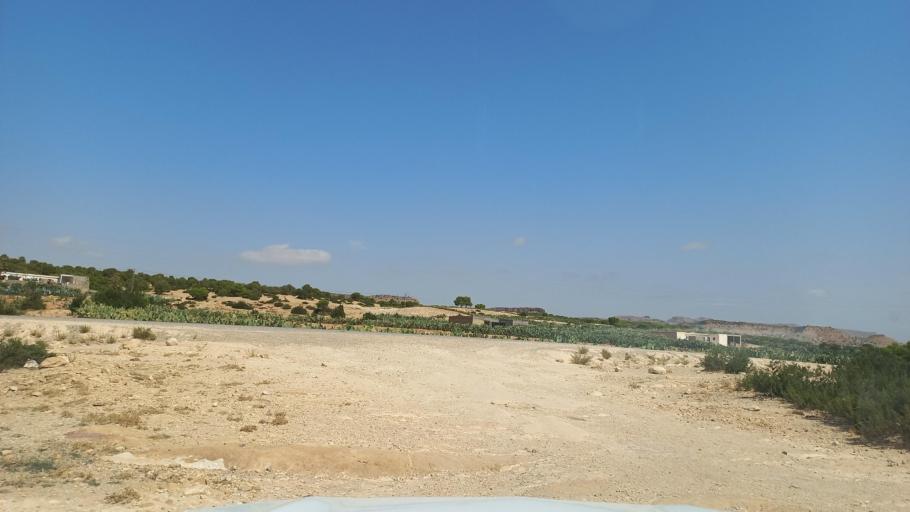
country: TN
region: Al Qasrayn
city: Sbiba
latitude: 35.3984
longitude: 8.9596
